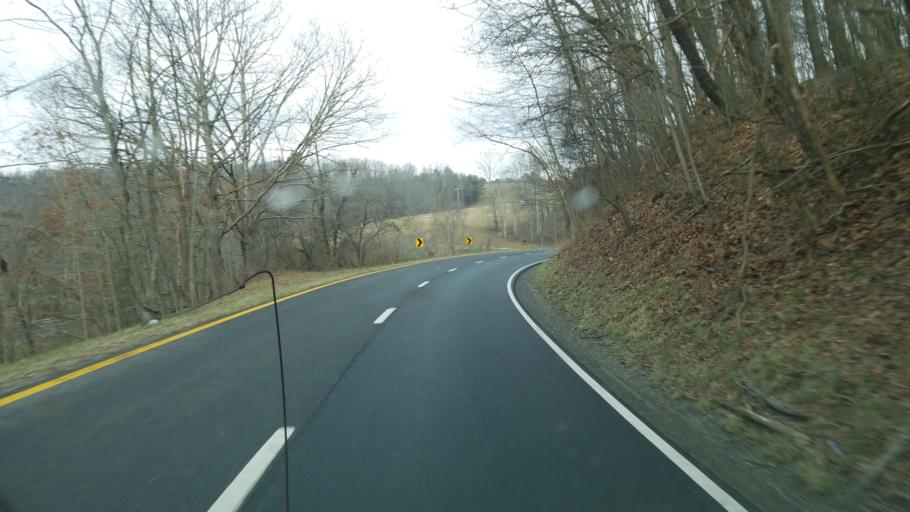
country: US
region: Virginia
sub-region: Giles County
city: Pearisburg
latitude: 37.2887
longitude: -80.7424
